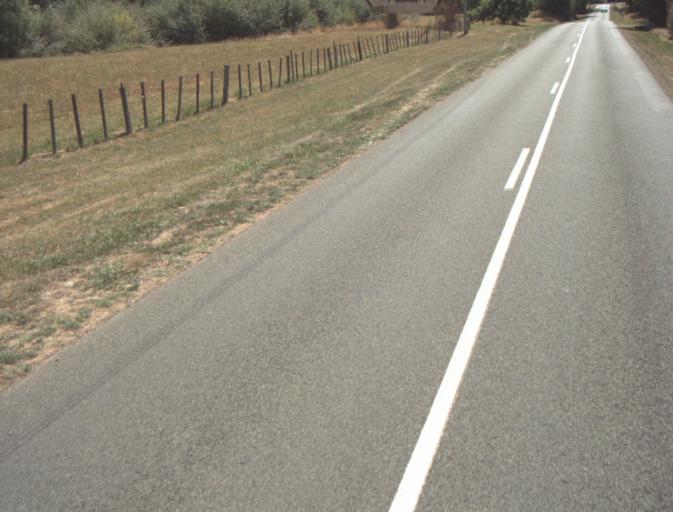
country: AU
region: Tasmania
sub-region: Launceston
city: Mayfield
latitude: -41.2631
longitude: 147.1351
